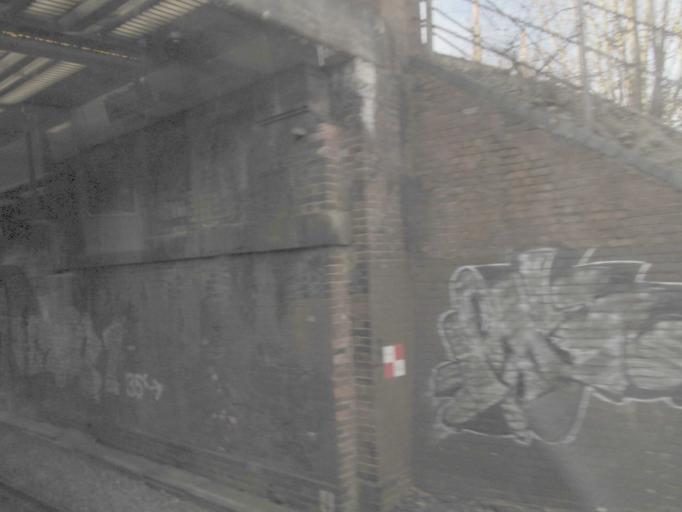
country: GB
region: England
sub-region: Hampshire
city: Farnborough
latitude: 51.2989
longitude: -0.7412
